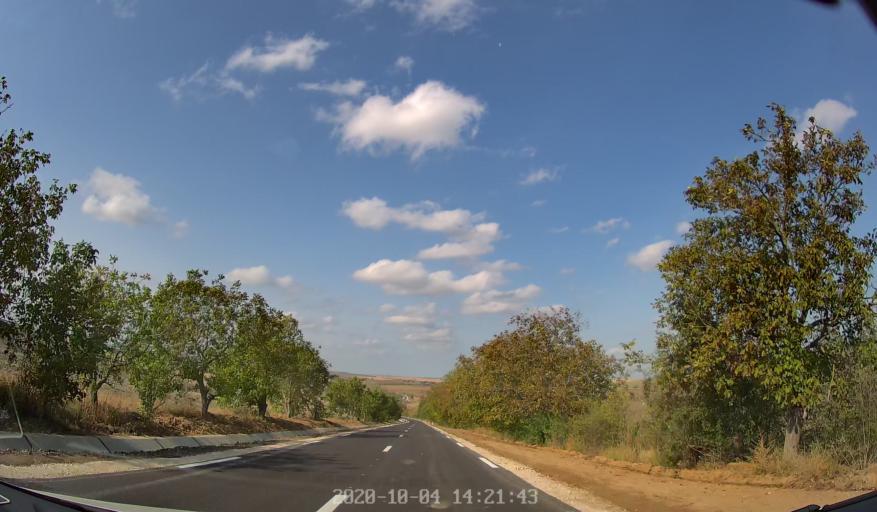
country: MD
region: Rezina
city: Saharna
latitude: 47.5885
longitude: 28.9539
